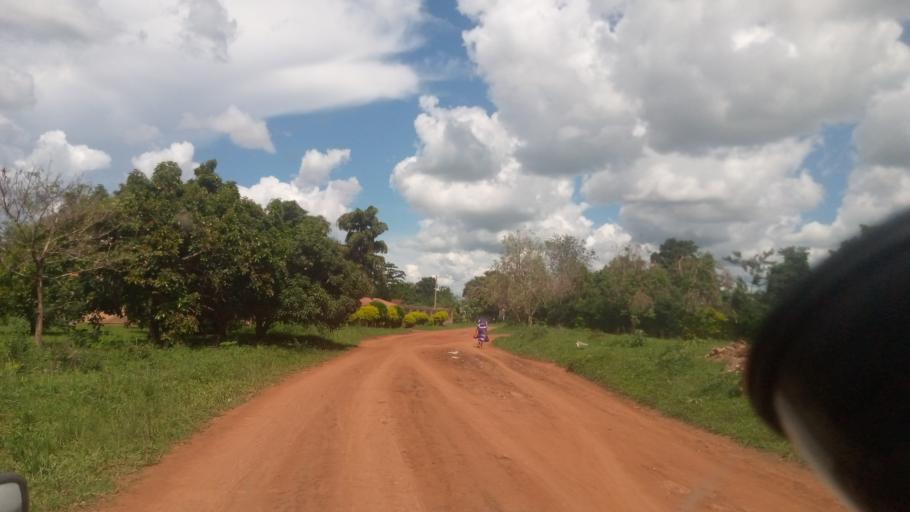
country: UG
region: Northern Region
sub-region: Lira District
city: Lira
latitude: 2.2378
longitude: 32.9058
